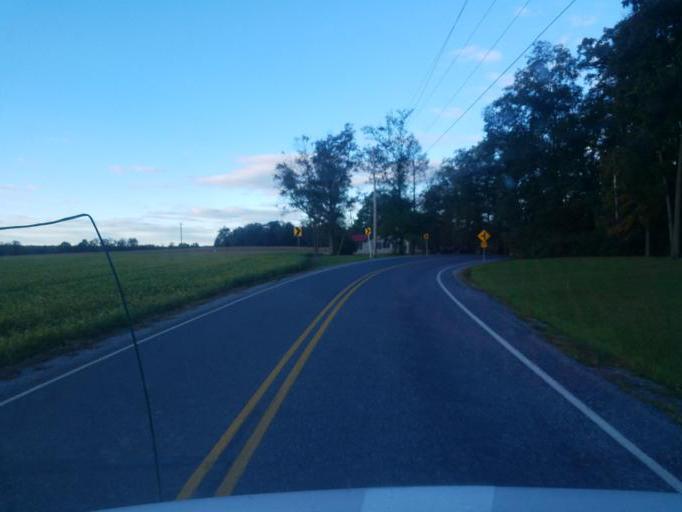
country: US
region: Pennsylvania
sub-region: Adams County
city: New Oxford
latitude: 39.9123
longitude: -77.0790
